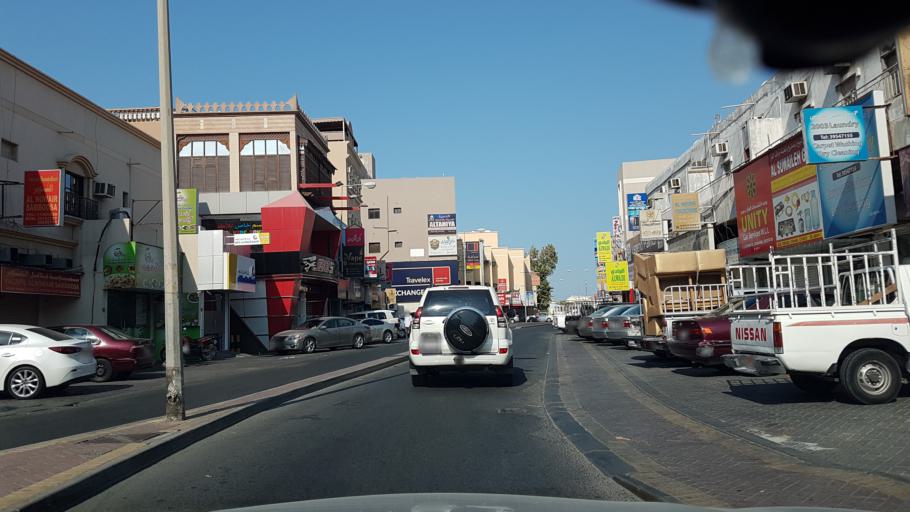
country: BH
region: Muharraq
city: Al Muharraq
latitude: 26.2560
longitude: 50.6340
